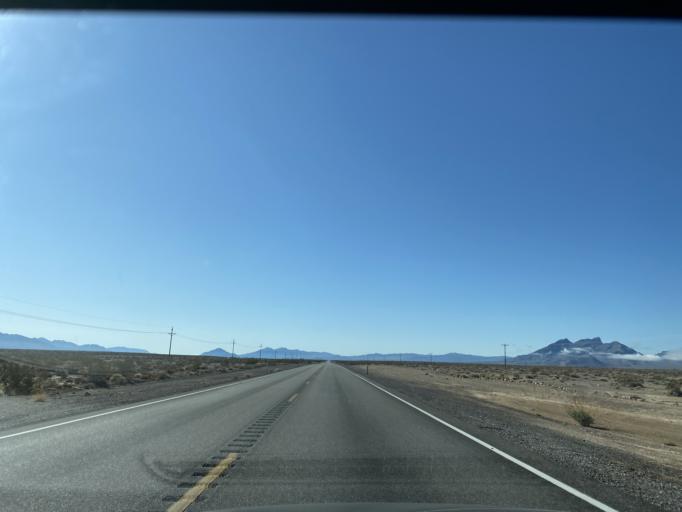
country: US
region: Nevada
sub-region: Nye County
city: Pahrump
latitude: 36.4786
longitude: -116.4216
